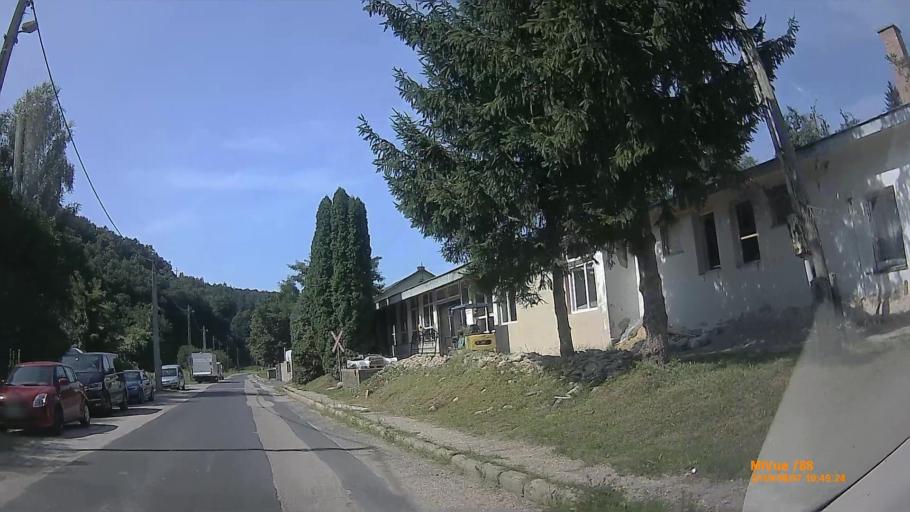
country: HU
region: Veszprem
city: Ajka
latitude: 47.0854
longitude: 17.5792
